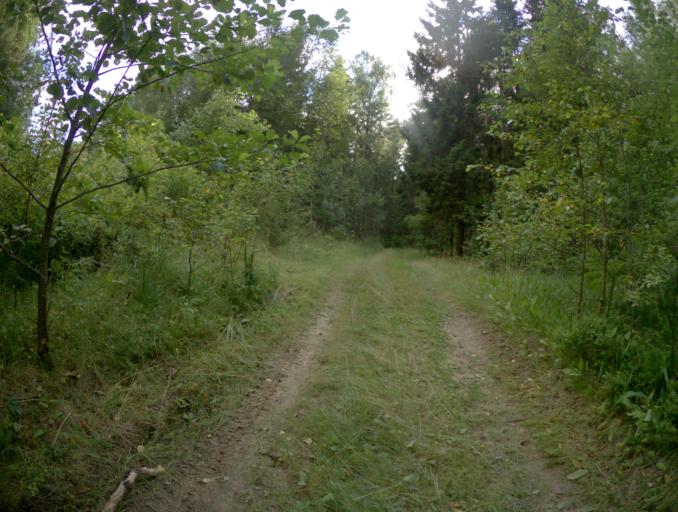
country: RU
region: Vladimir
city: Orgtrud
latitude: 56.1258
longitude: 40.5721
